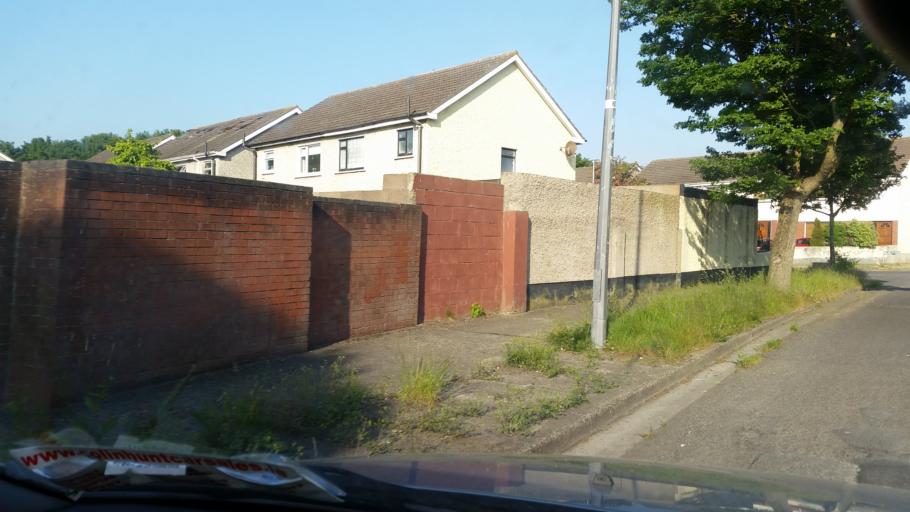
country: IE
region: Leinster
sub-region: Fingal County
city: Blanchardstown
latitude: 53.4009
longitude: -6.3710
